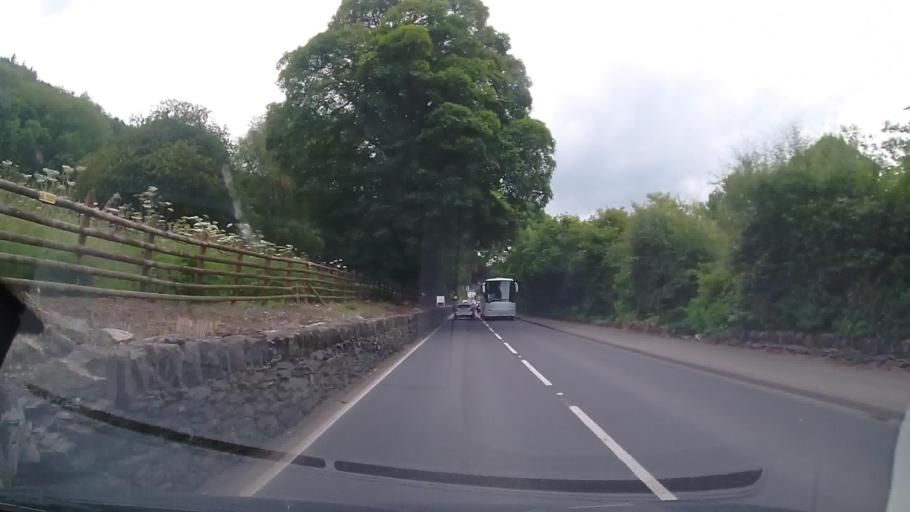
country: GB
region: Wales
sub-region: Denbighshire
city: Corwen
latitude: 52.9812
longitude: -3.3640
